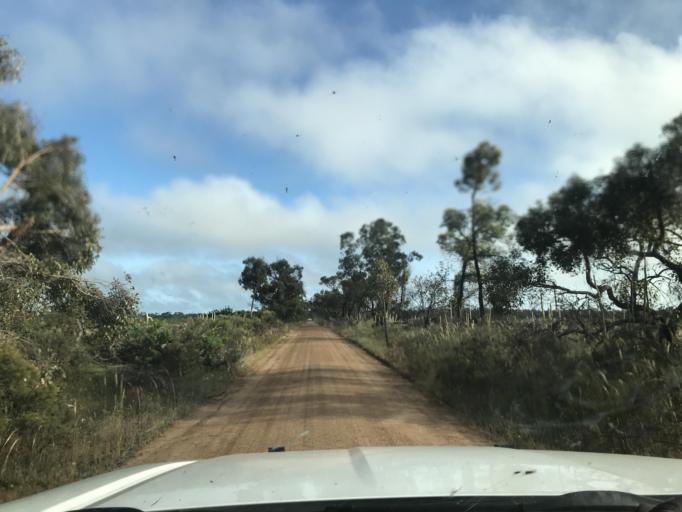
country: AU
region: South Australia
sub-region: Wattle Range
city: Penola
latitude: -37.1899
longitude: 141.1835
